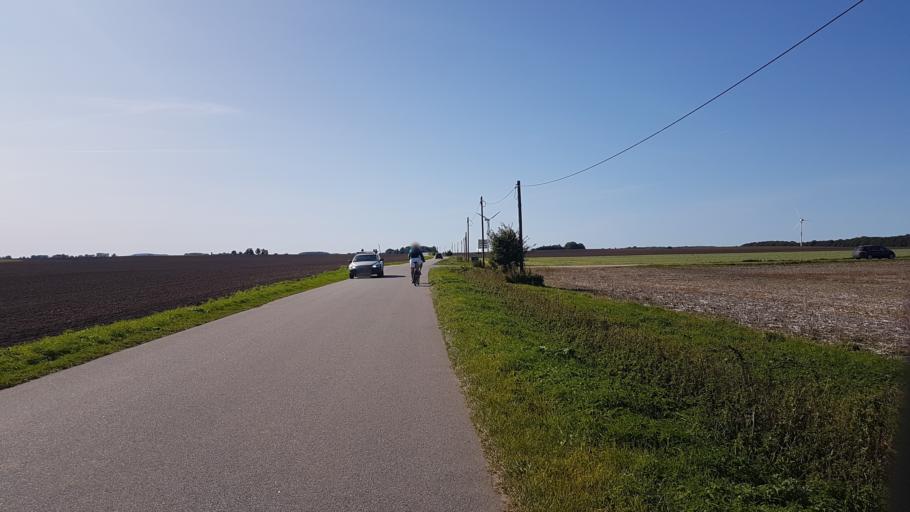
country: DE
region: Mecklenburg-Vorpommern
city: Altenkirchen
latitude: 54.6599
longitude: 13.3395
